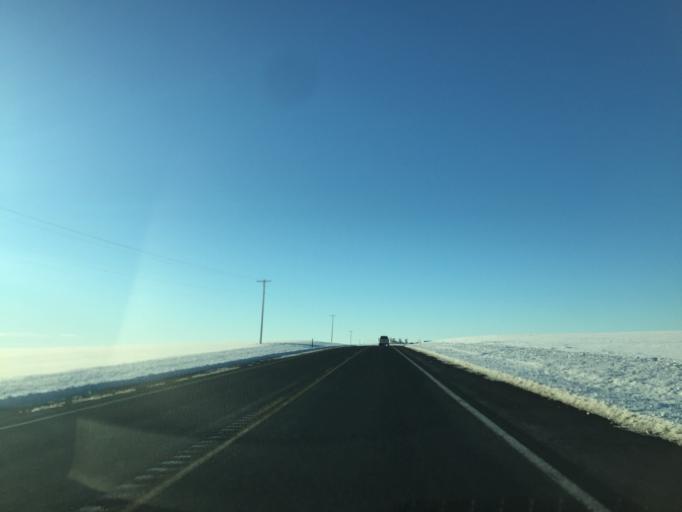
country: US
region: Washington
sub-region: Okanogan County
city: Coulee Dam
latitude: 47.6845
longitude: -119.0029
